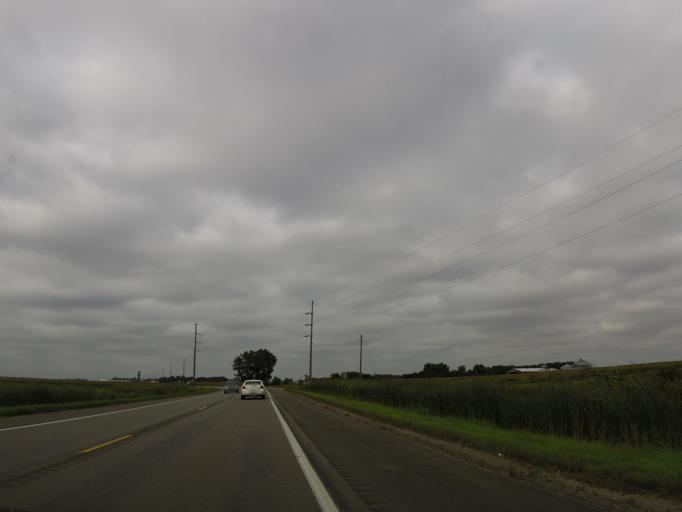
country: US
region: Minnesota
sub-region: Renville County
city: Olivia
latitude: 44.7883
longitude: -95.0677
